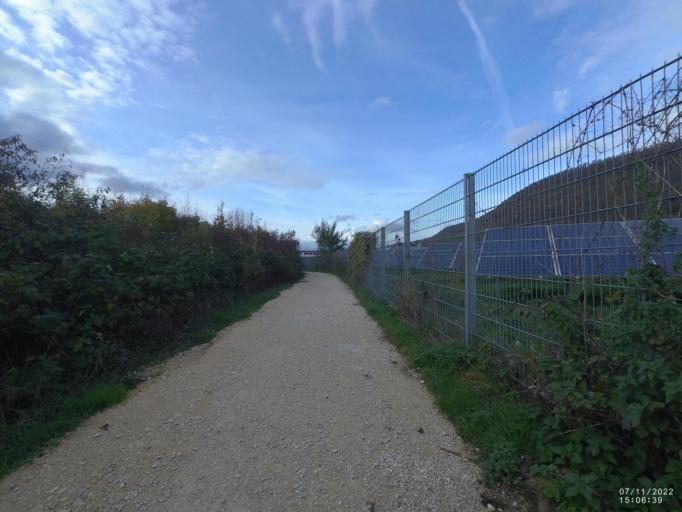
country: DE
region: Baden-Wuerttemberg
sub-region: Regierungsbezirk Stuttgart
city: Kuchen
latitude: 48.6309
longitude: 9.8122
